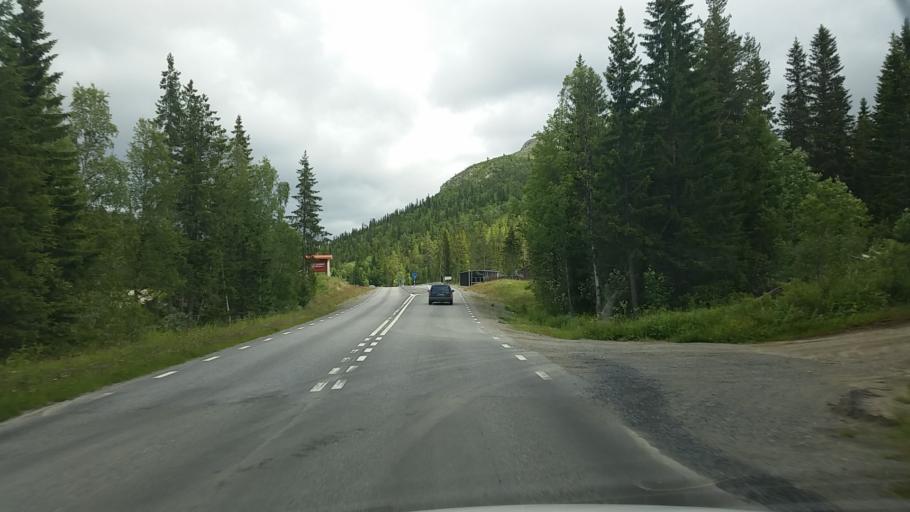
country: SE
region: Jaemtland
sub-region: Bergs Kommun
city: Hoverberg
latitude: 62.4936
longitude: 13.9391
